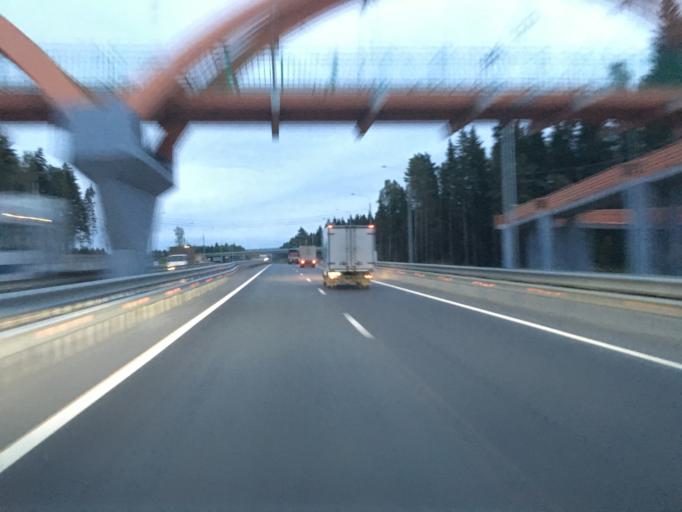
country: RU
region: Kaluga
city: Maloyaroslavets
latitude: 54.9242
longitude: 36.4043
